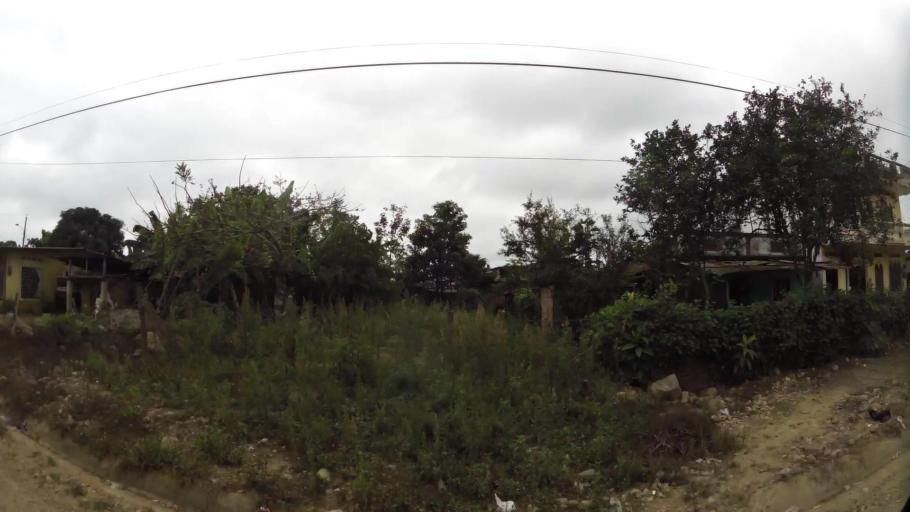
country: EC
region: El Oro
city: Pasaje
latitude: -3.2367
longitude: -79.8246
